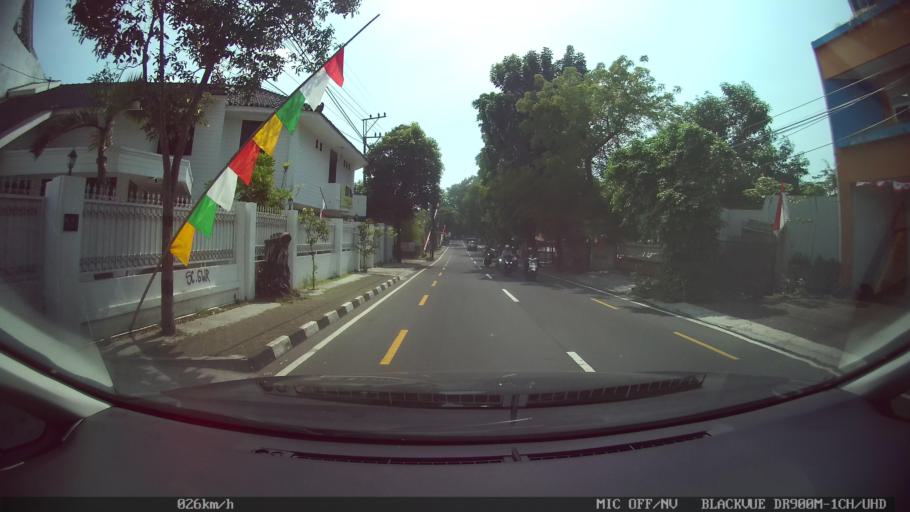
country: ID
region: Daerah Istimewa Yogyakarta
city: Yogyakarta
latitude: -7.8090
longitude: 110.3932
